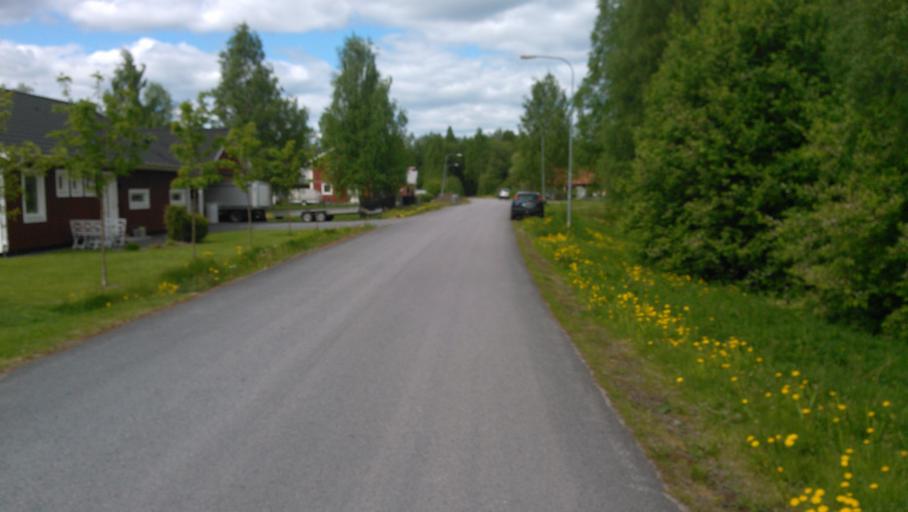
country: SE
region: Vaesterbotten
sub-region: Umea Kommun
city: Roback
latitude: 63.8768
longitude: 20.0538
